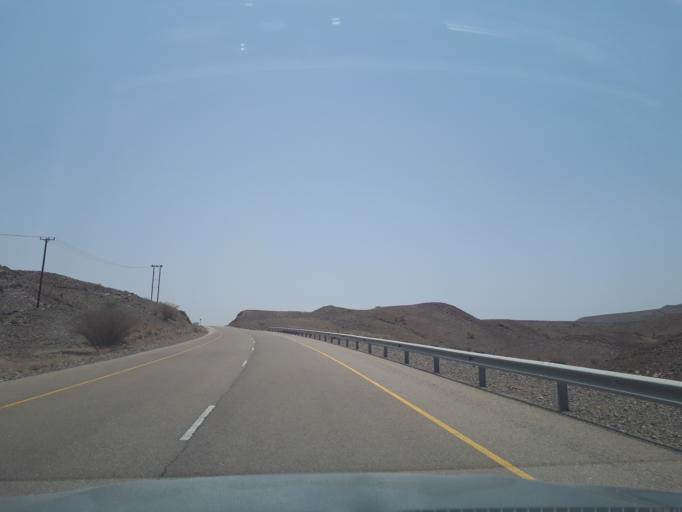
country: OM
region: Ash Sharqiyah
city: Badiyah
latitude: 22.5011
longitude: 59.1081
